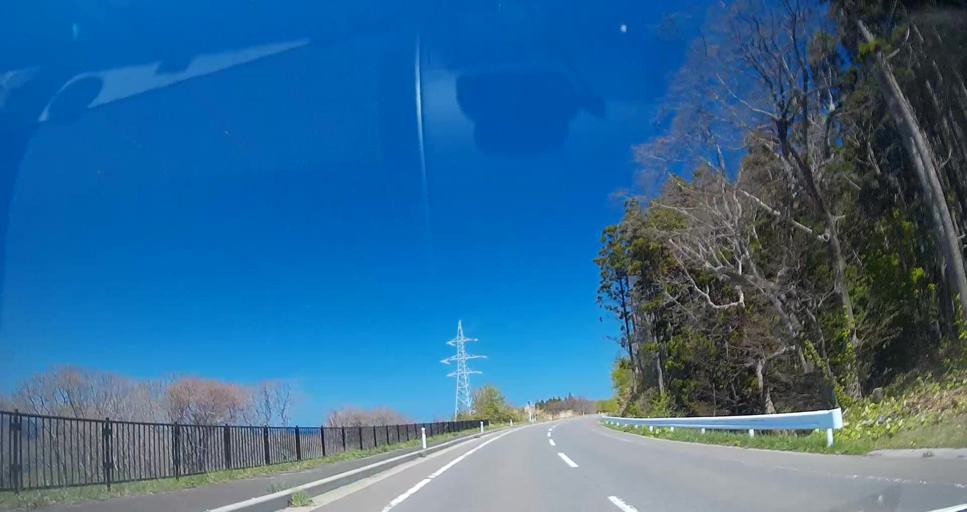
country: JP
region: Aomori
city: Mutsu
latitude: 41.3879
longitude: 141.4111
